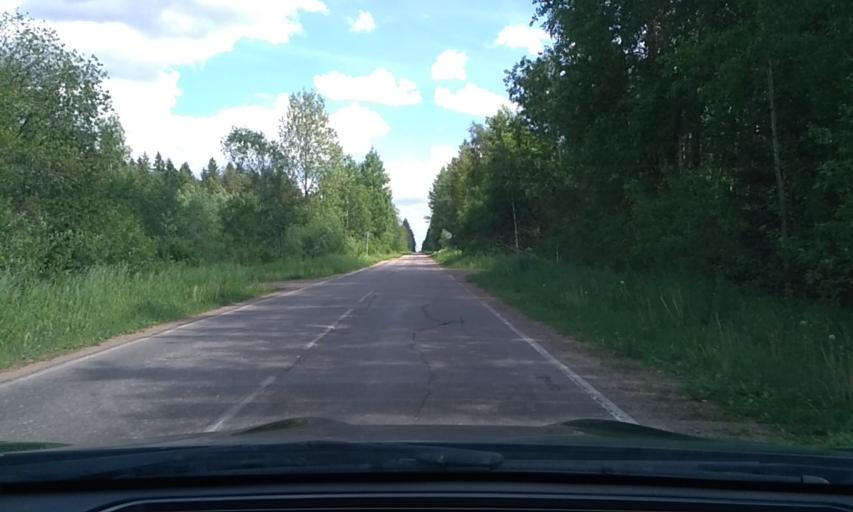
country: RU
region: Leningrad
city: Otradnoye
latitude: 59.8228
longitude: 30.7465
